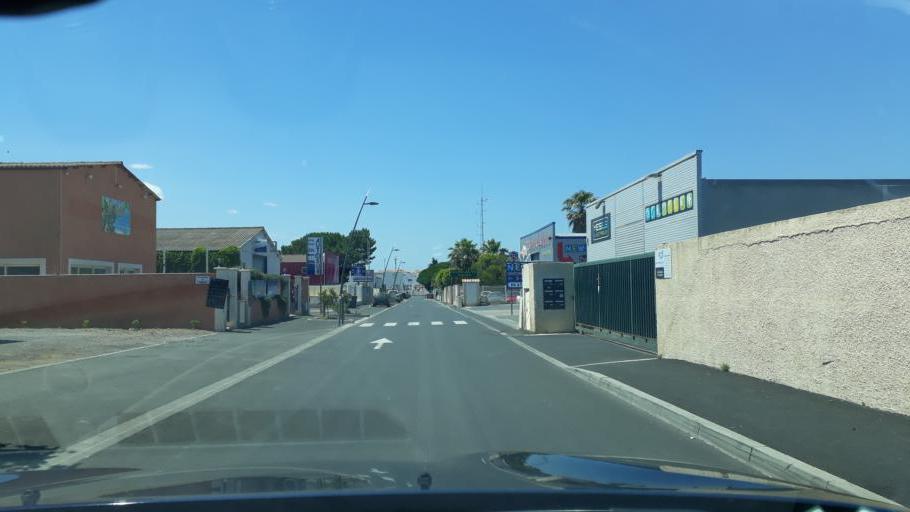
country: FR
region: Languedoc-Roussillon
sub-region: Departement de l'Herault
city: Agde
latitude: 43.3093
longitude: 3.4953
